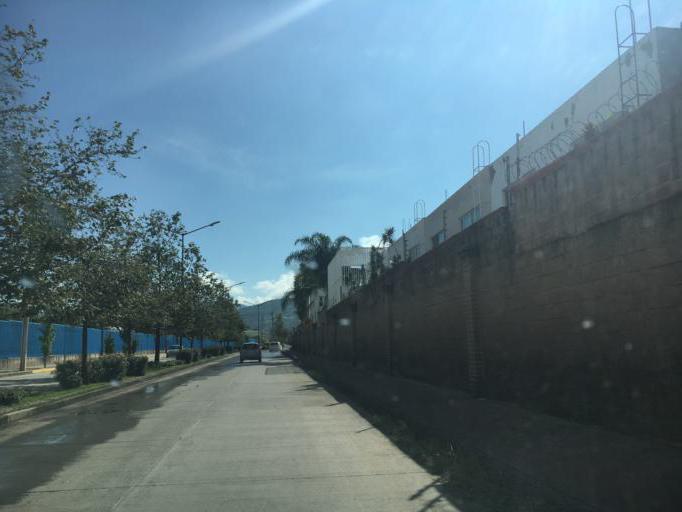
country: MX
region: Guanajuato
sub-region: Leon
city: Medina
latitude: 21.1258
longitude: -101.6222
